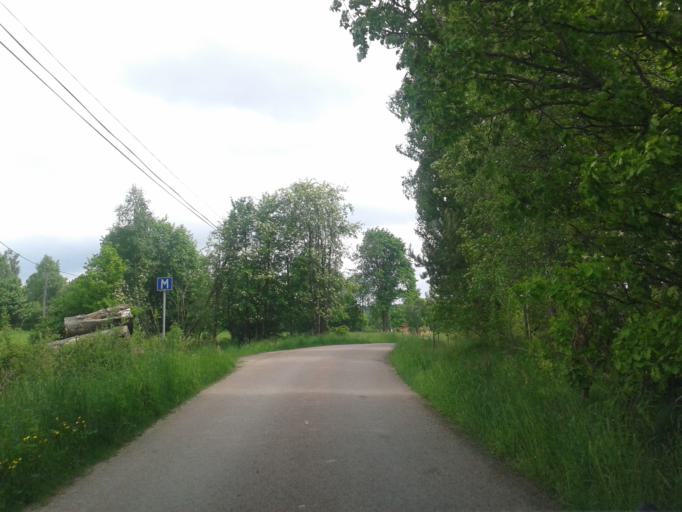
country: SE
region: Vaestra Goetaland
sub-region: Kungalvs Kommun
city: Kungalv
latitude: 57.9042
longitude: 11.9474
